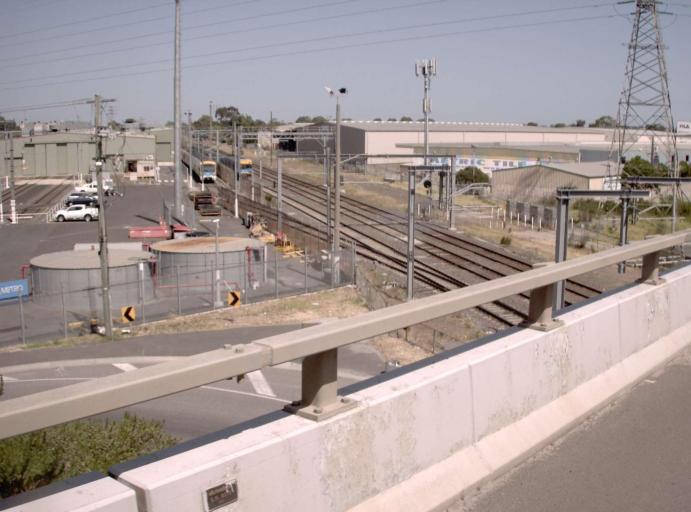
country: AU
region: Victoria
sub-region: Greater Dandenong
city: Springvale
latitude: -37.9394
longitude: 145.1403
